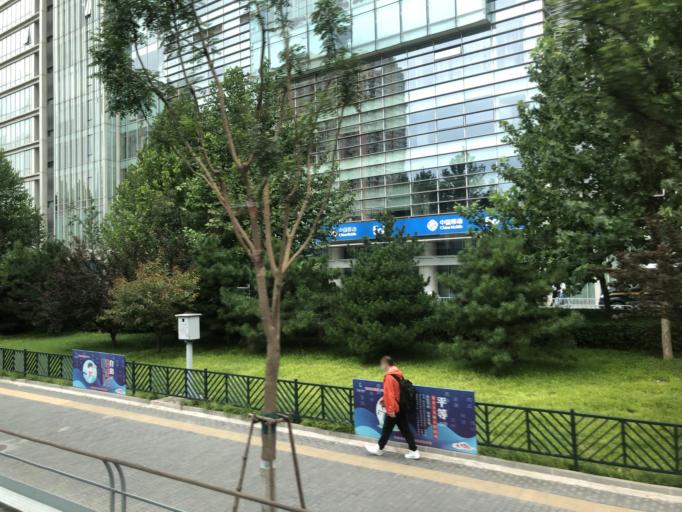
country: CN
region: Beijing
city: Jinrongjie
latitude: 39.9339
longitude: 116.3189
